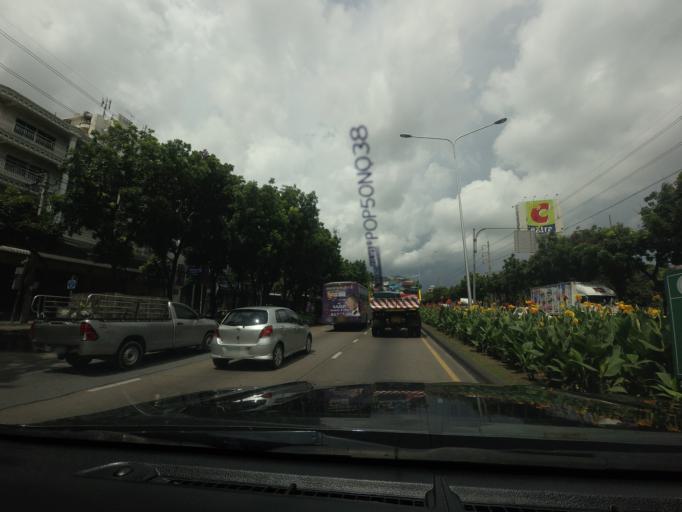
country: TH
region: Bangkok
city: Nong Khaem
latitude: 13.7073
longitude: 100.3687
